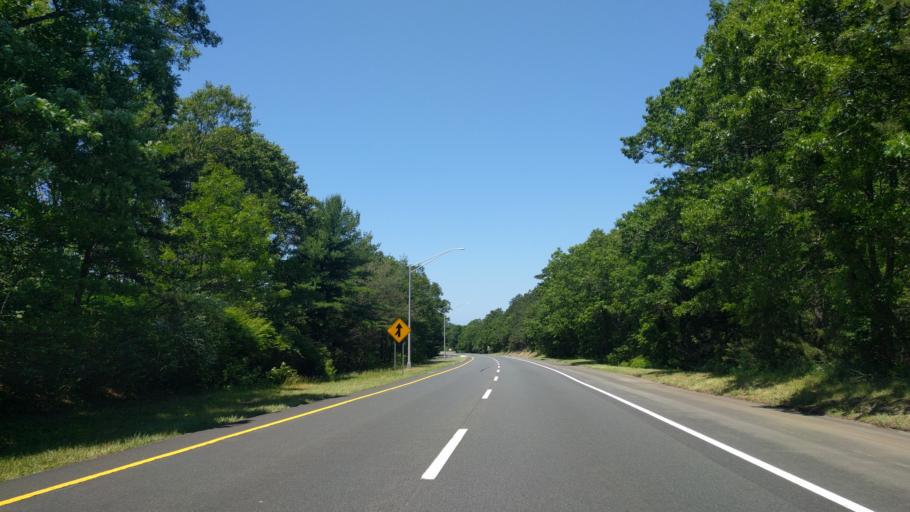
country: US
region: New York
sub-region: Suffolk County
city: Manorville
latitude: 40.8599
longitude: -72.7637
